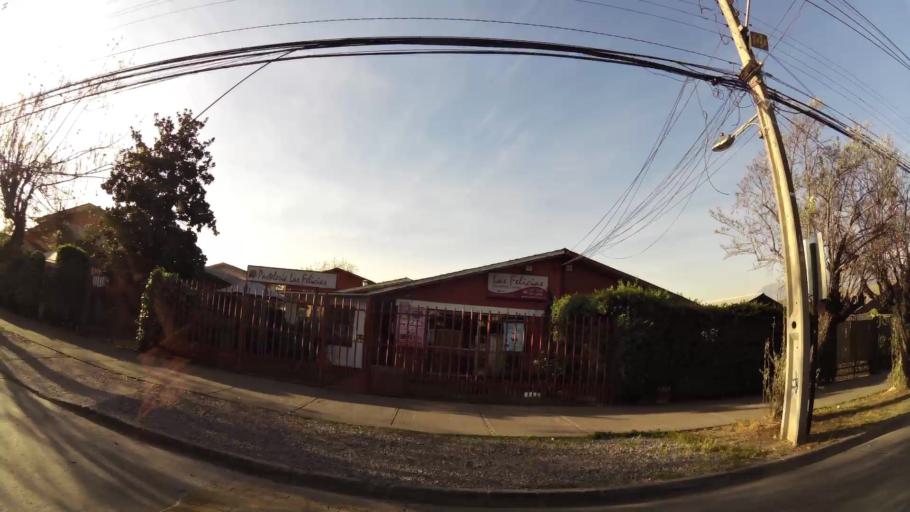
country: CL
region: Santiago Metropolitan
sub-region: Provincia de Cordillera
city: Puente Alto
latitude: -33.5436
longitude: -70.5729
